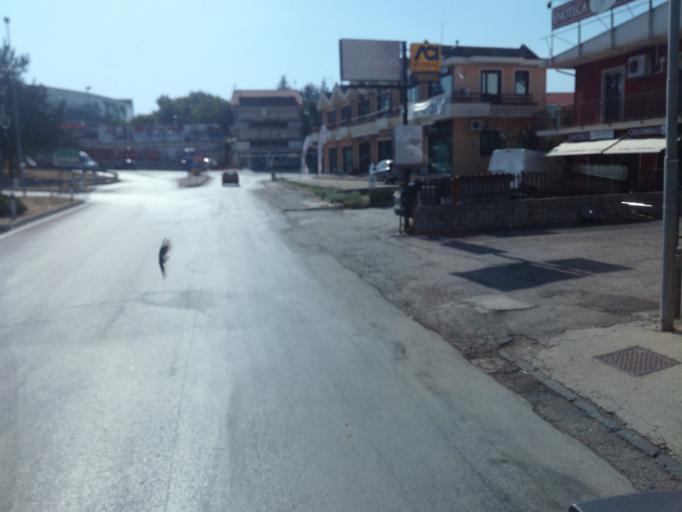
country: IT
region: Campania
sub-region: Provincia di Avellino
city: Grottaminarda
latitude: 41.0666
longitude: 15.0603
